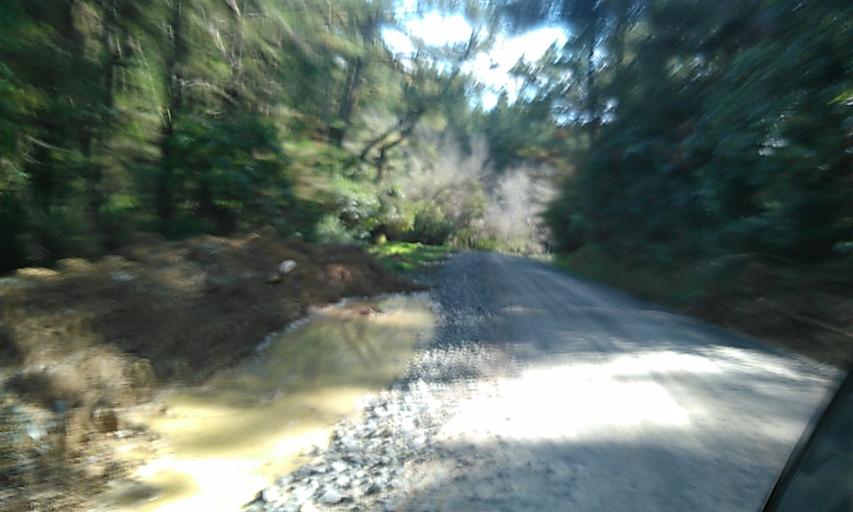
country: NZ
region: Gisborne
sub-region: Gisborne District
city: Gisborne
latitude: -38.2147
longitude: 178.0671
